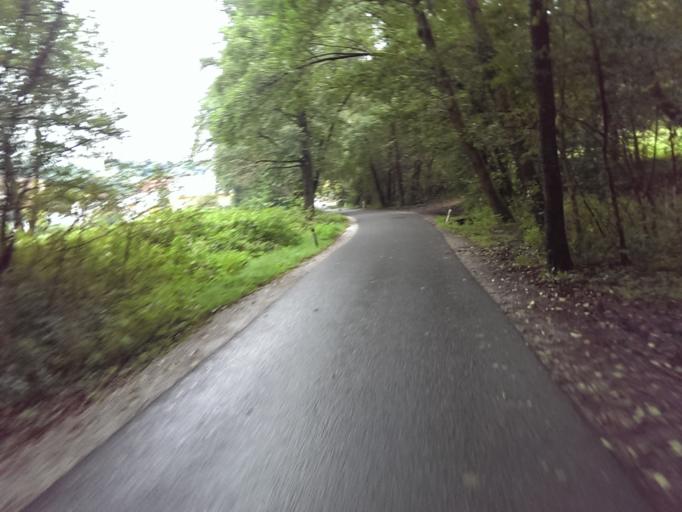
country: AT
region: Styria
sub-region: Politischer Bezirk Graz-Umgebung
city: Hart bei Graz
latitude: 47.0642
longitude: 15.4987
